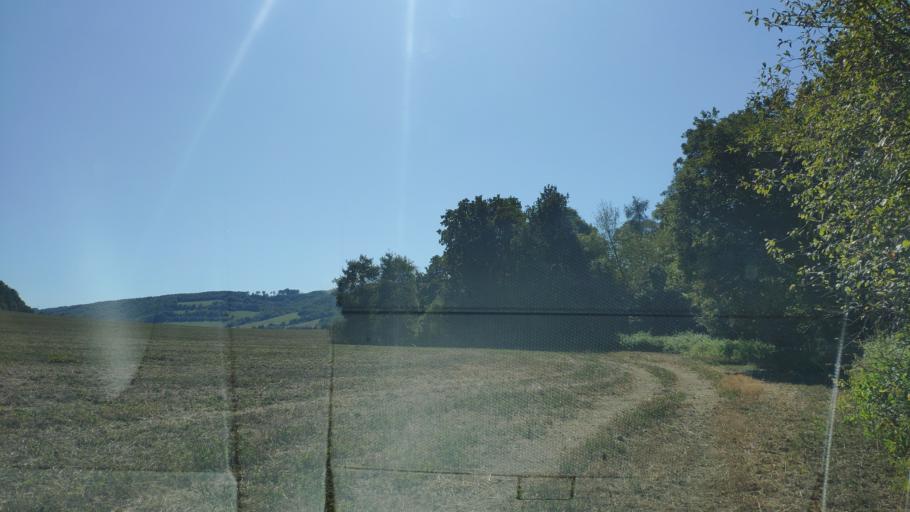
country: SK
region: Presovsky
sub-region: Okres Presov
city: Presov
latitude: 48.9729
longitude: 21.1377
